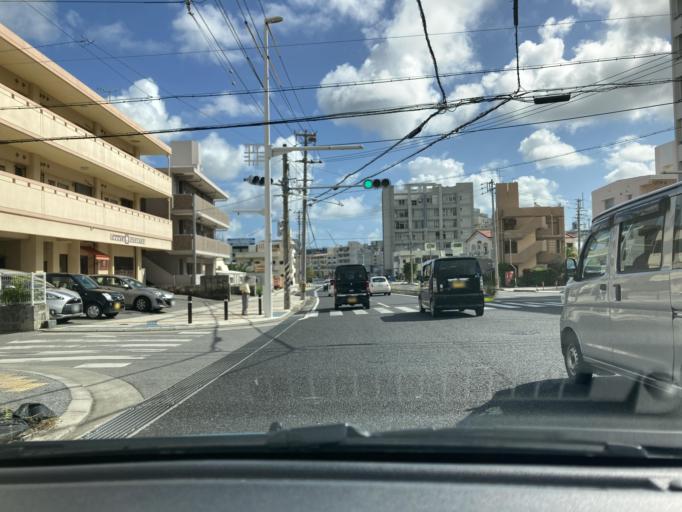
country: JP
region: Okinawa
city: Tomigusuku
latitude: 26.1978
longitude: 127.7268
